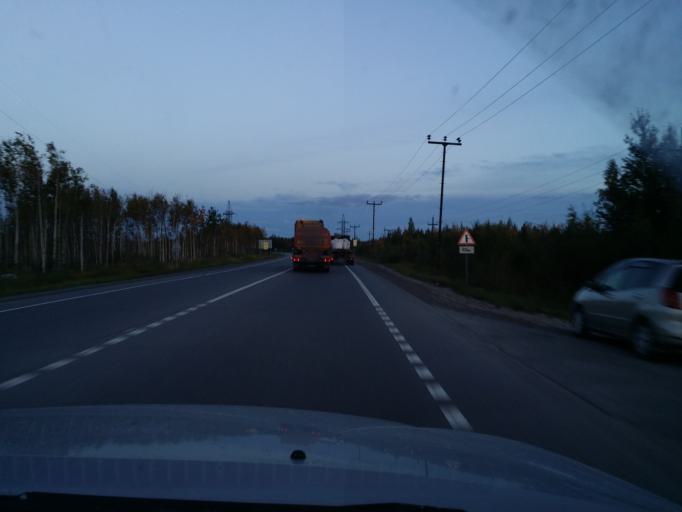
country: RU
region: Khanty-Mansiyskiy Avtonomnyy Okrug
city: Nizhnevartovsk
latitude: 61.0300
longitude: 76.3625
